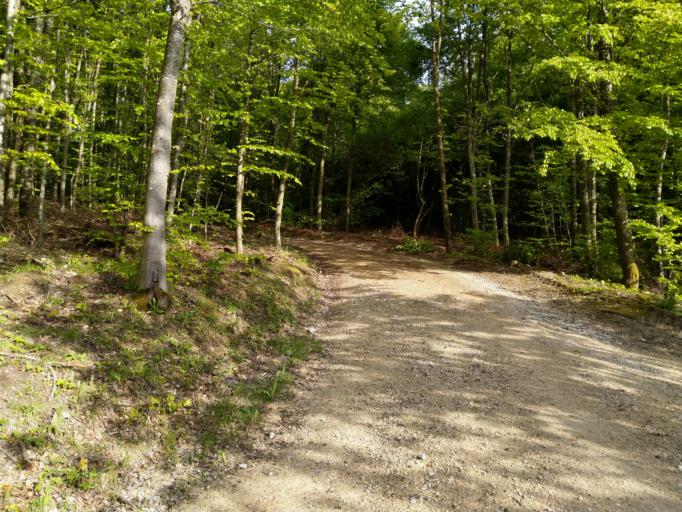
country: CH
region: Aargau
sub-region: Bezirk Kulm
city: Schoftland
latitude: 47.3139
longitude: 8.0574
